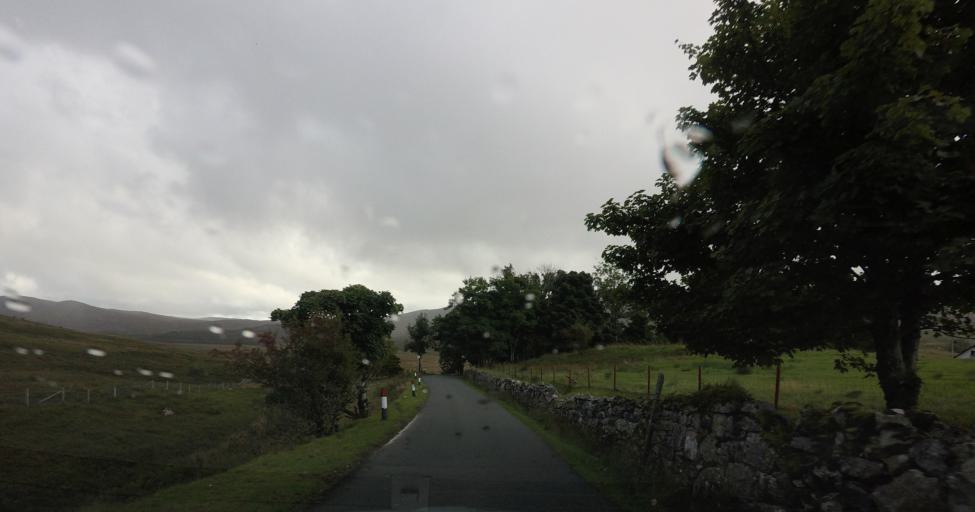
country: GB
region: Scotland
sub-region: Highland
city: Portree
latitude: 57.2109
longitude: -5.9893
